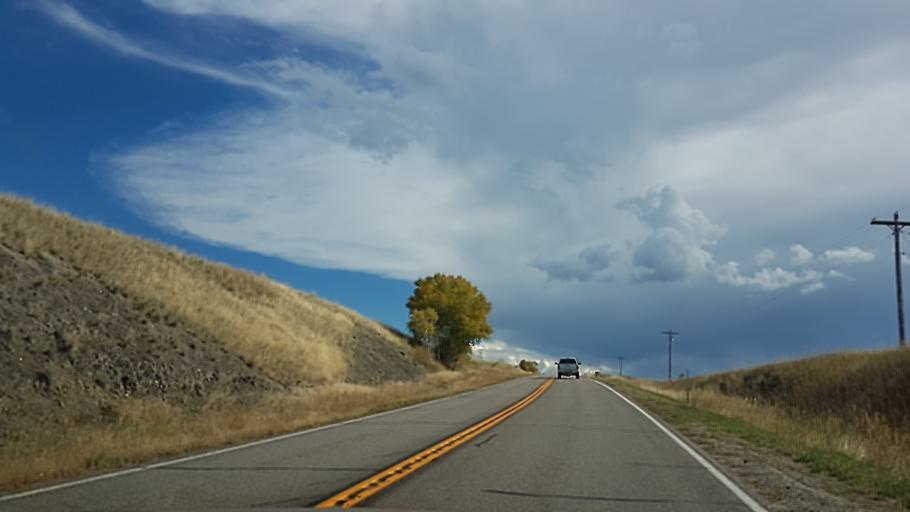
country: US
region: Montana
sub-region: Jefferson County
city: Whitehall
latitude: 45.8016
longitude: -111.9246
